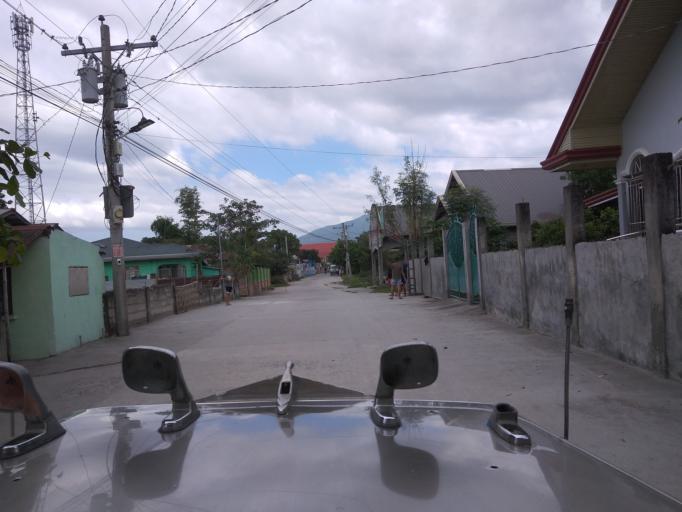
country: PH
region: Central Luzon
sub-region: Province of Pampanga
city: Anao
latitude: 15.1173
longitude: 120.6978
